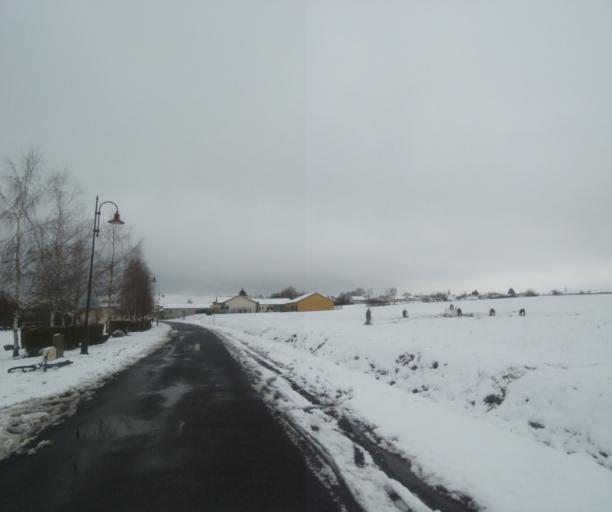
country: FR
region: Champagne-Ardenne
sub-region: Departement de la Haute-Marne
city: Laneuville-a-Remy
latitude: 48.5077
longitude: 4.8707
